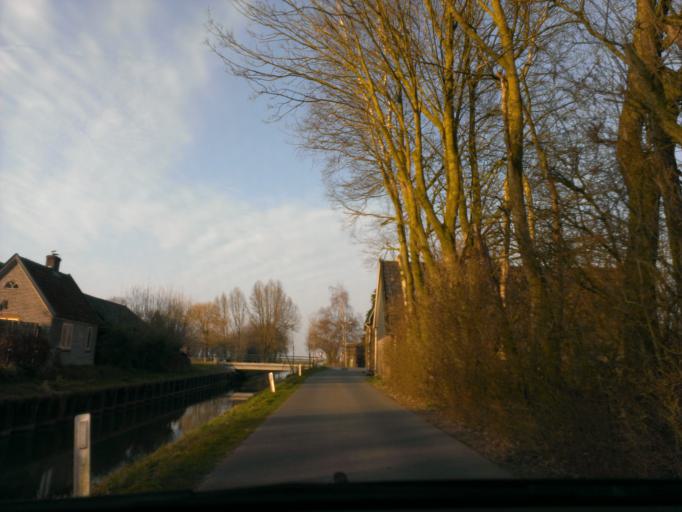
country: NL
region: Gelderland
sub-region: Gemeente Epe
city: Oene
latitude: 52.3519
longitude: 6.0606
